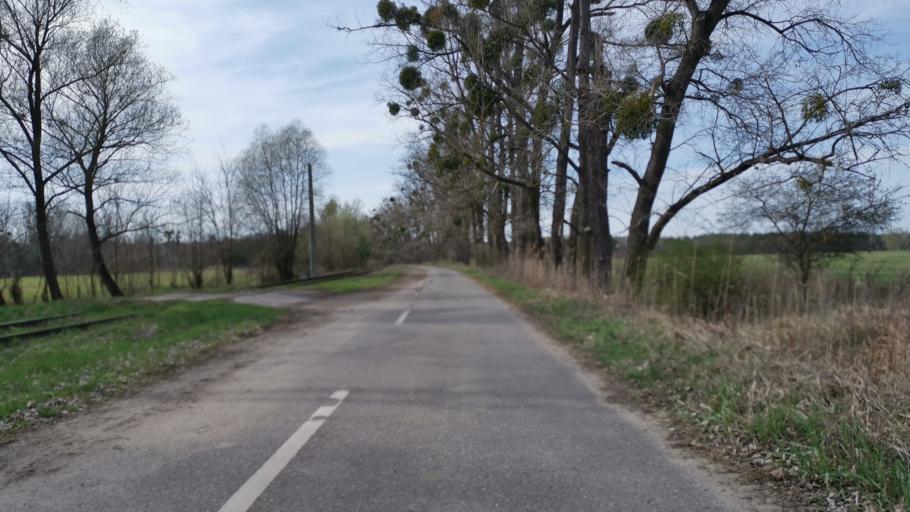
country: SK
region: Trnavsky
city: Gbely
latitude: 48.6637
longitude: 17.0677
